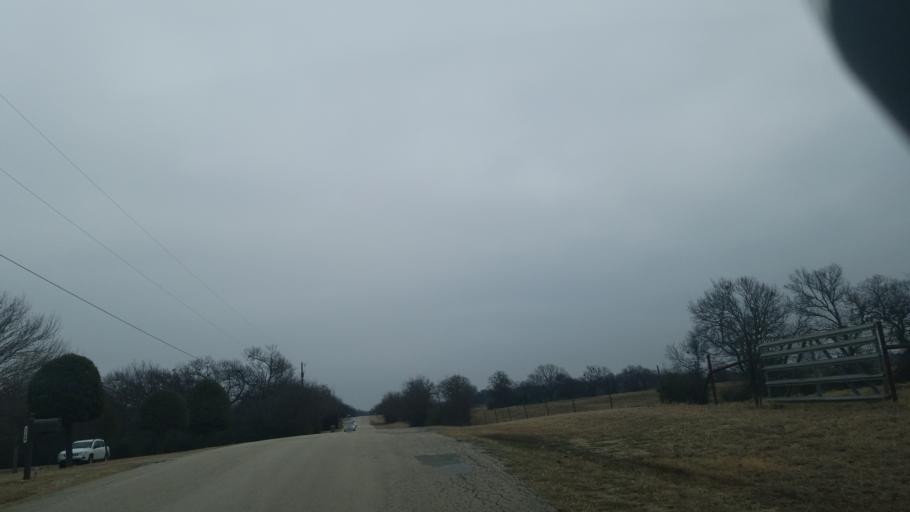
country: US
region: Texas
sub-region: Denton County
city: Argyle
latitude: 33.1472
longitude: -97.1540
